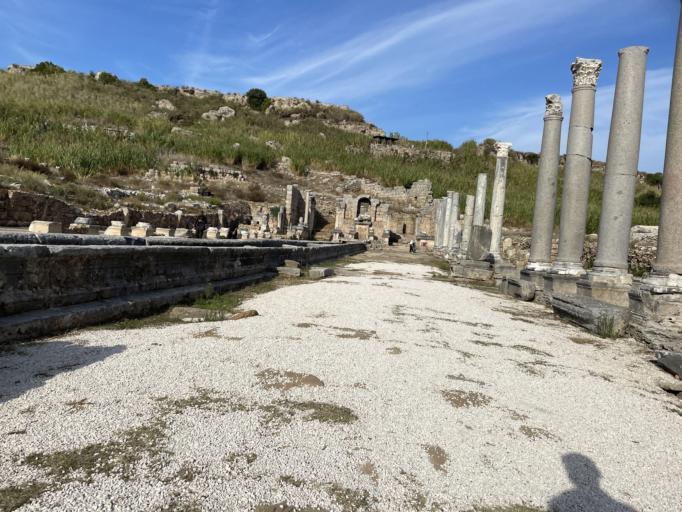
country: TR
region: Antalya
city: Aksu
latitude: 36.9654
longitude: 30.8549
